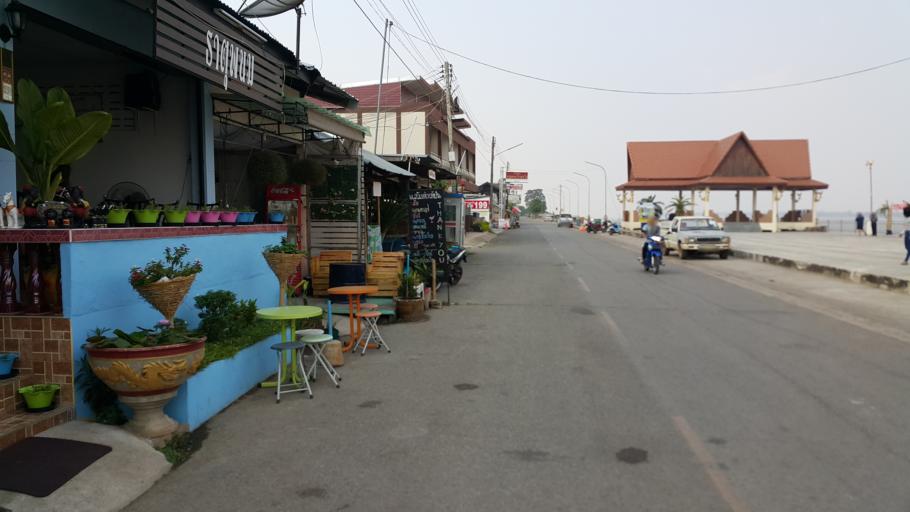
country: TH
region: Nakhon Phanom
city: That Phanom
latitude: 16.9449
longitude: 104.7296
